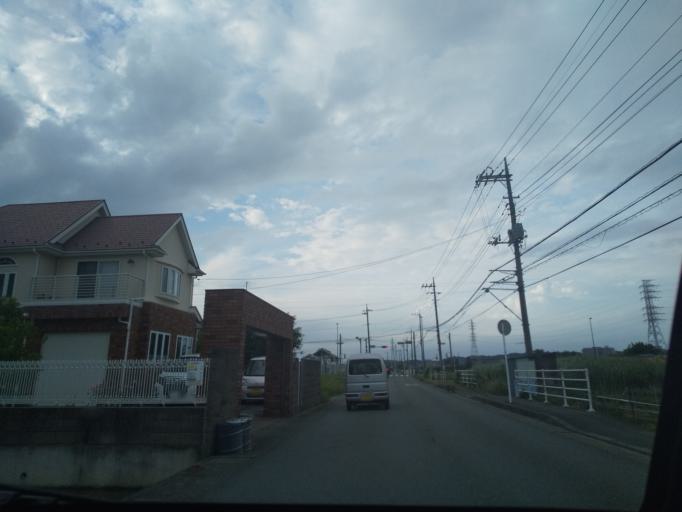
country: JP
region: Kanagawa
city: Zama
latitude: 35.4857
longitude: 139.3854
